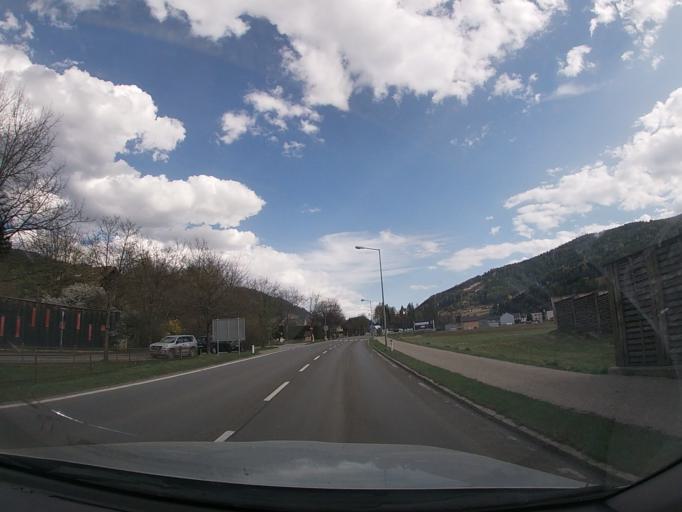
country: AT
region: Styria
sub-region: Politischer Bezirk Murau
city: Sankt Lorenzen bei Scheifling
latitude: 47.1483
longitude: 14.4143
